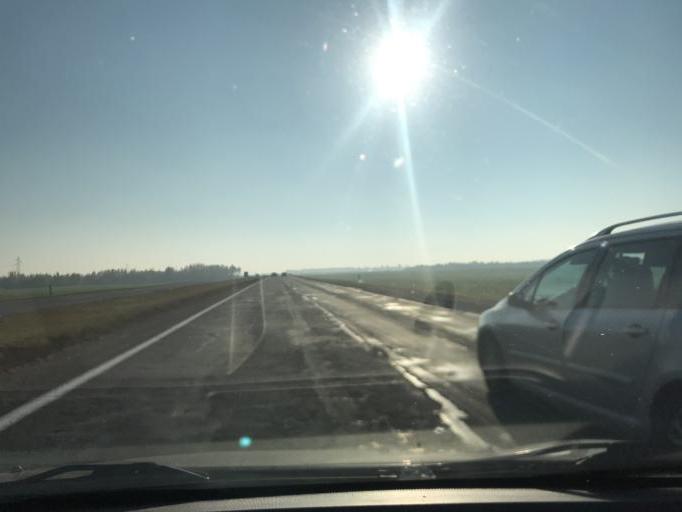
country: BY
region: Minsk
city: Dukora
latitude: 53.6480
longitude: 27.9792
